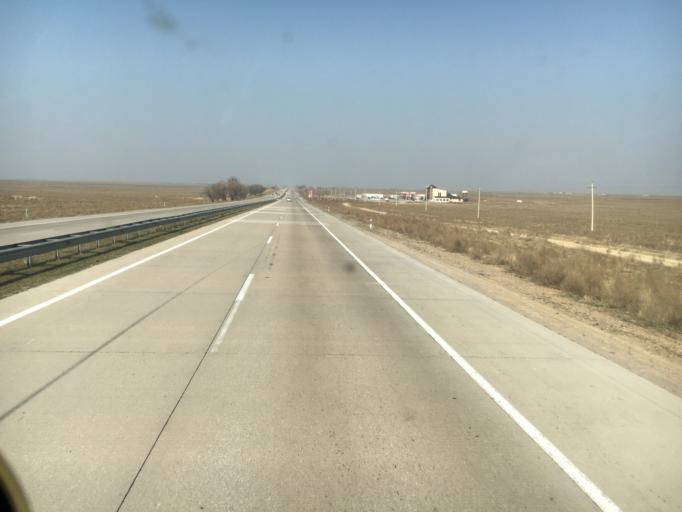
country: KZ
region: Ongtustik Qazaqstan
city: Temirlanovka
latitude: 42.8381
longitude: 69.1117
